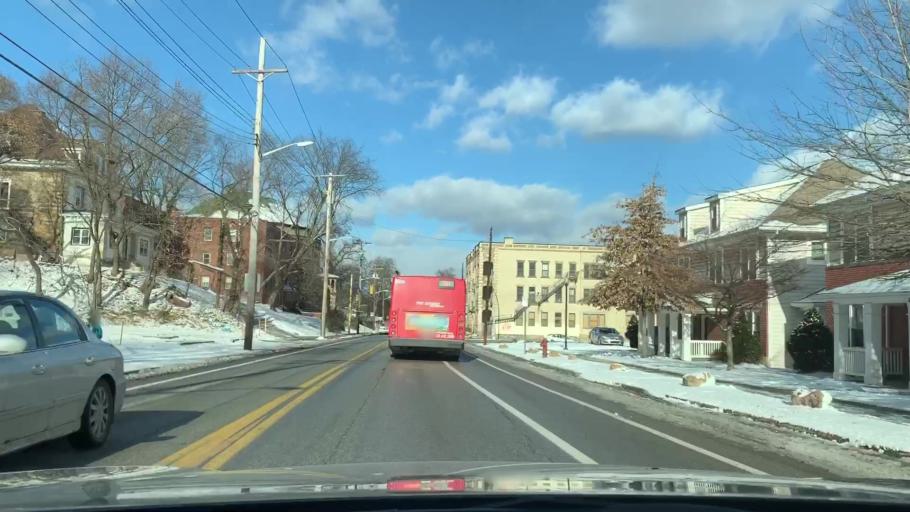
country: US
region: Pennsylvania
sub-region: Allegheny County
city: Bloomfield
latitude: 40.4649
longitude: -79.9299
